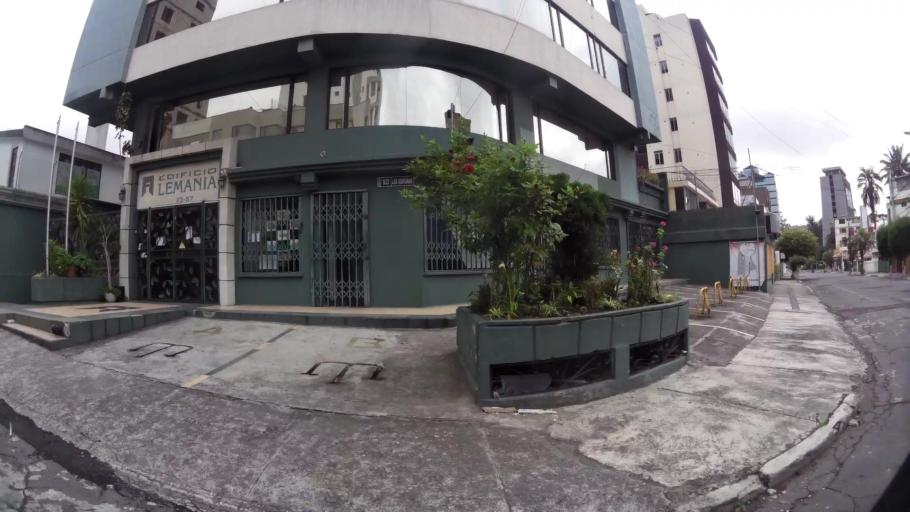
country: EC
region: Pichincha
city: Quito
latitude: -0.1870
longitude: -78.4896
